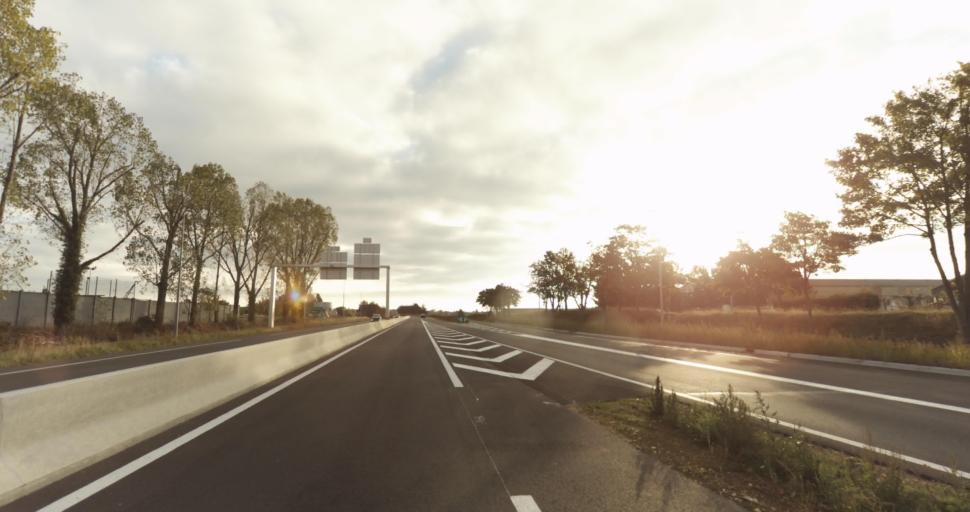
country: FR
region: Centre
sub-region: Departement d'Eure-et-Loir
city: Vernouillet
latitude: 48.7157
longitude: 1.3711
